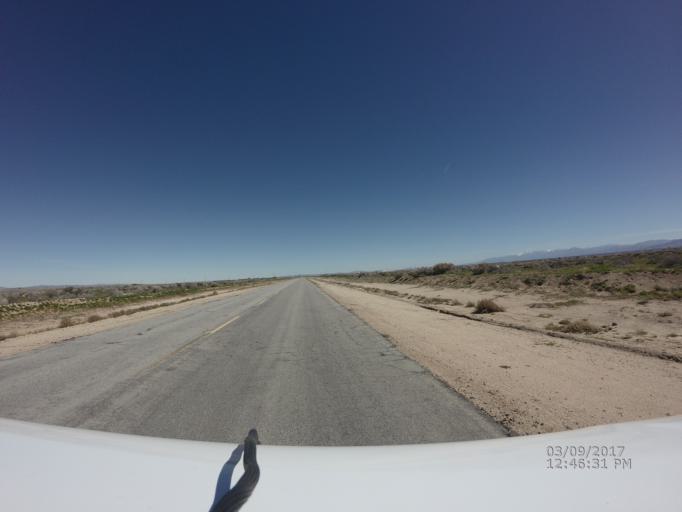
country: US
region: California
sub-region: Los Angeles County
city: Quartz Hill
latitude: 34.7475
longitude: -118.2633
